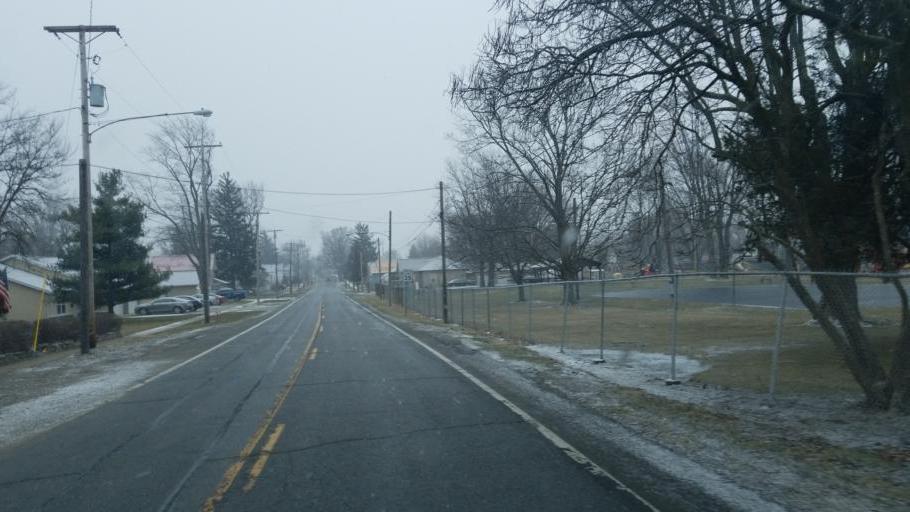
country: US
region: Ohio
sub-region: Defiance County
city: Hicksville
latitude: 41.2978
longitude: -84.7695
